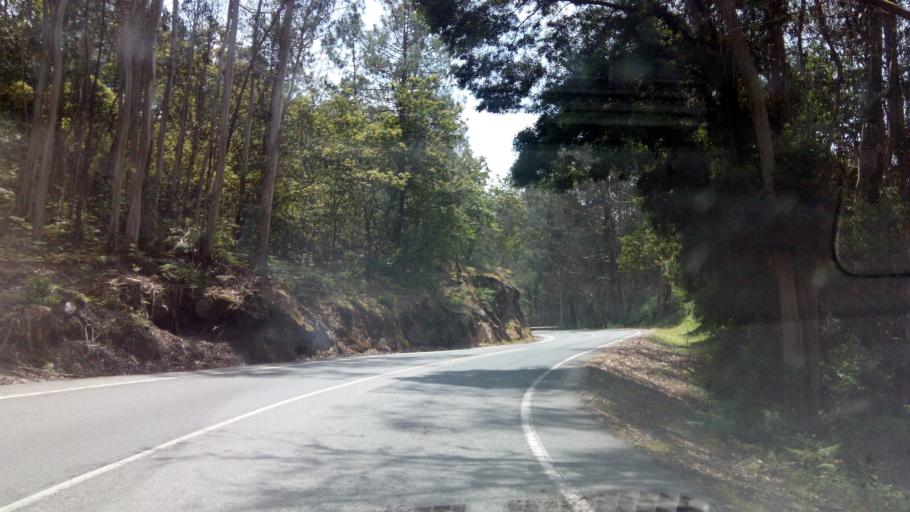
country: ES
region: Galicia
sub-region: Provincia de Pontevedra
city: Marin
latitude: 42.3426
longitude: -8.7099
